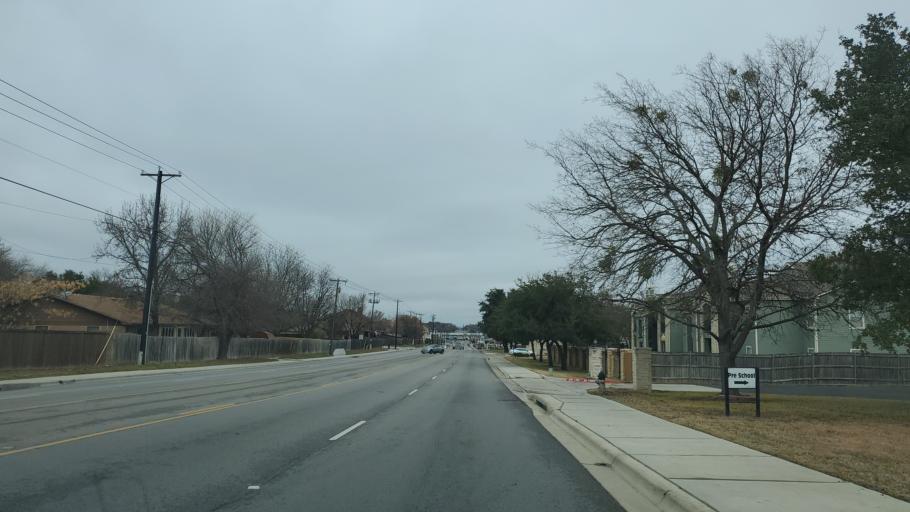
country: US
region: Texas
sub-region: Bell County
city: Killeen
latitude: 31.0871
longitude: -97.7352
